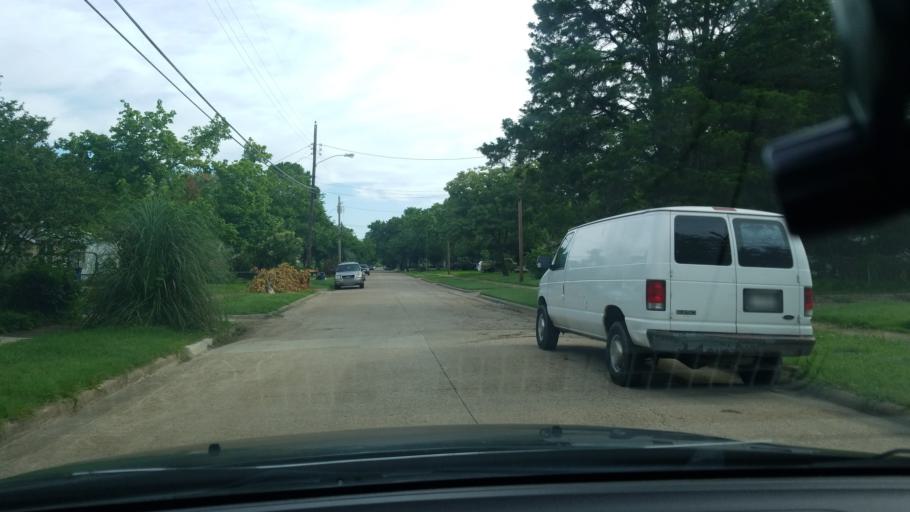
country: US
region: Texas
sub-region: Dallas County
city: Balch Springs
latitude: 32.7580
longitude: -96.6668
